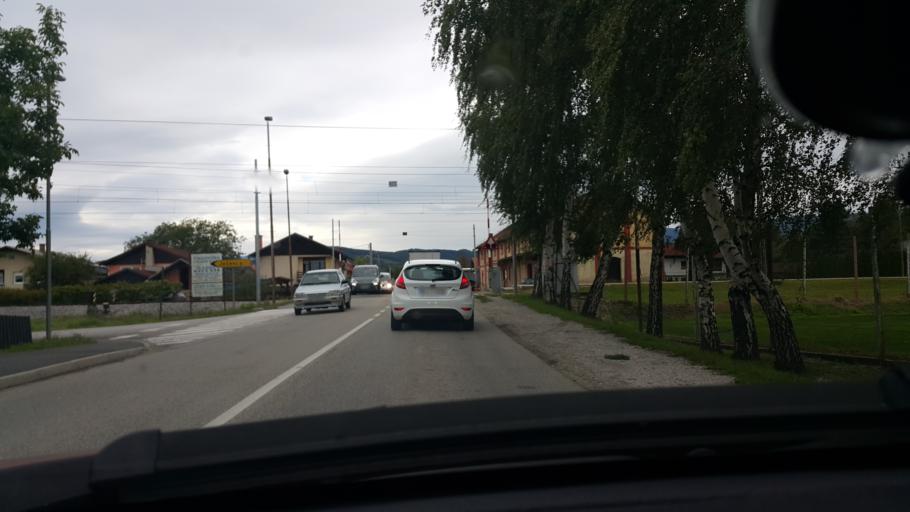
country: SI
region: Hoce-Slivnica
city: Hotinja Vas
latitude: 46.4523
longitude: 15.6645
